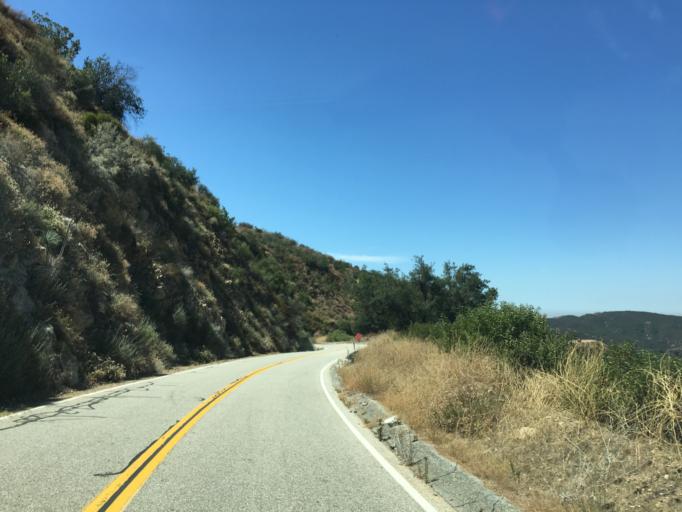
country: US
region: California
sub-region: Los Angeles County
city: Glendora
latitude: 34.1890
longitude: -117.8413
